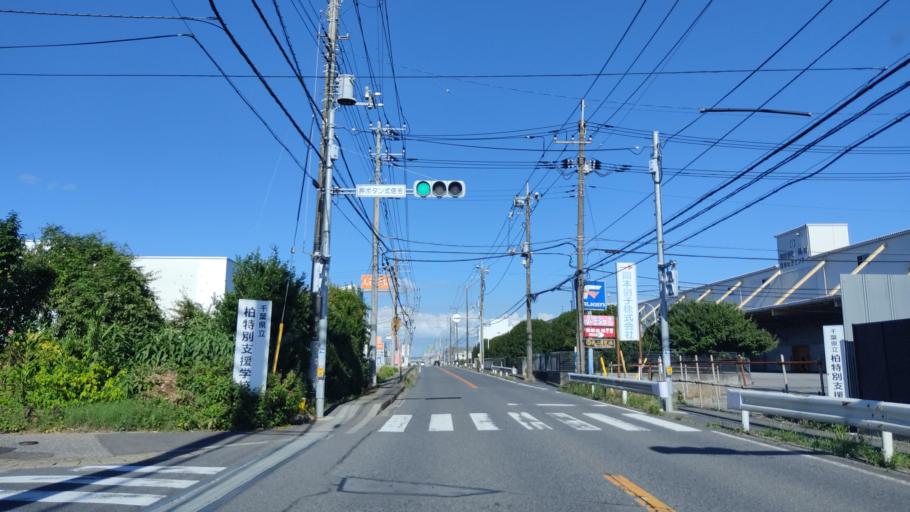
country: JP
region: Chiba
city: Kashiwa
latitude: 35.8876
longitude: 139.9409
